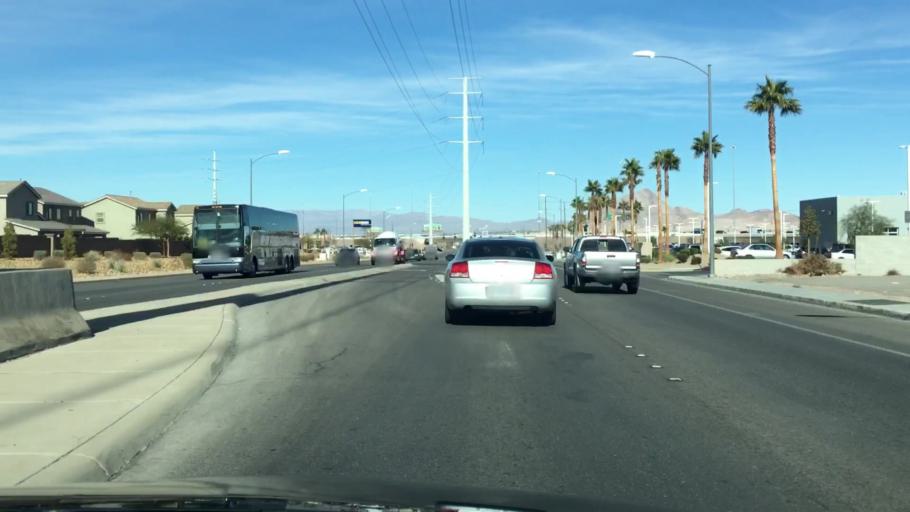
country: US
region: Nevada
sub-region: Clark County
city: Henderson
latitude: 36.0538
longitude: -115.0287
